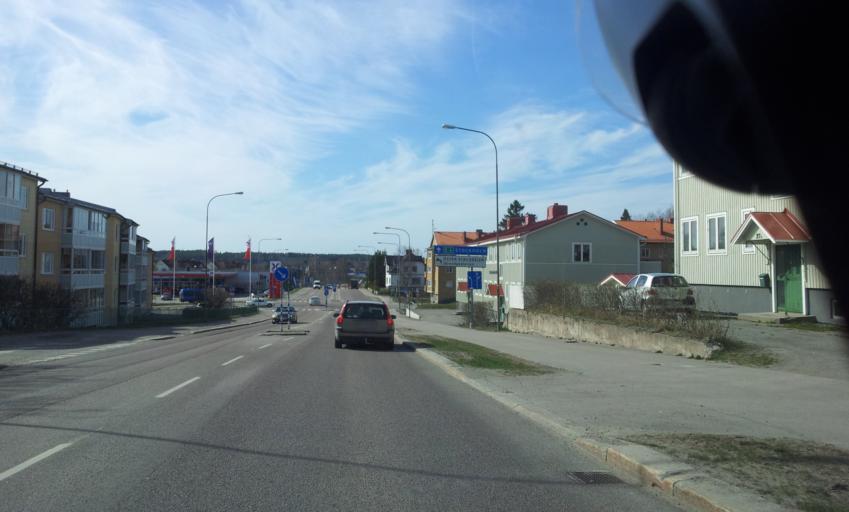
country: SE
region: Gaevleborg
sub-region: Hudiksvalls Kommun
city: Hudiksvall
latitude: 61.7205
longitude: 17.0991
